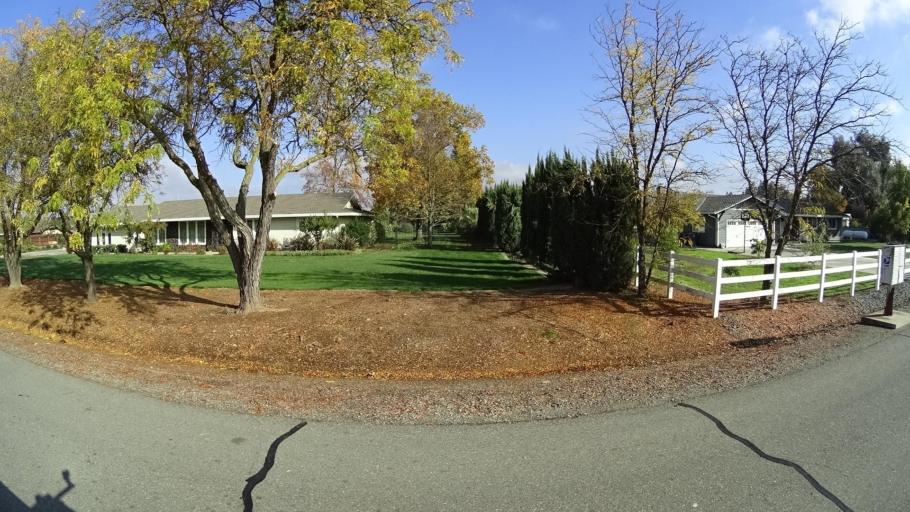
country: US
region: California
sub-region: Sacramento County
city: Vineyard
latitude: 38.4396
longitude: -121.3577
